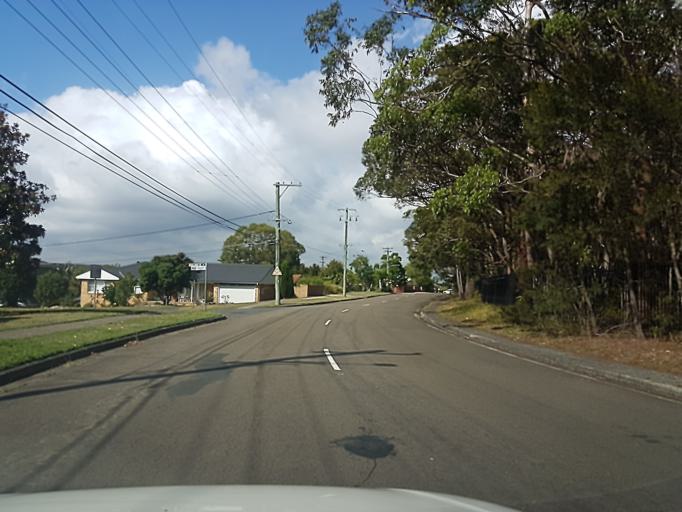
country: AU
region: New South Wales
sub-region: Warringah
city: Davidson
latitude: -33.7449
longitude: 151.2074
